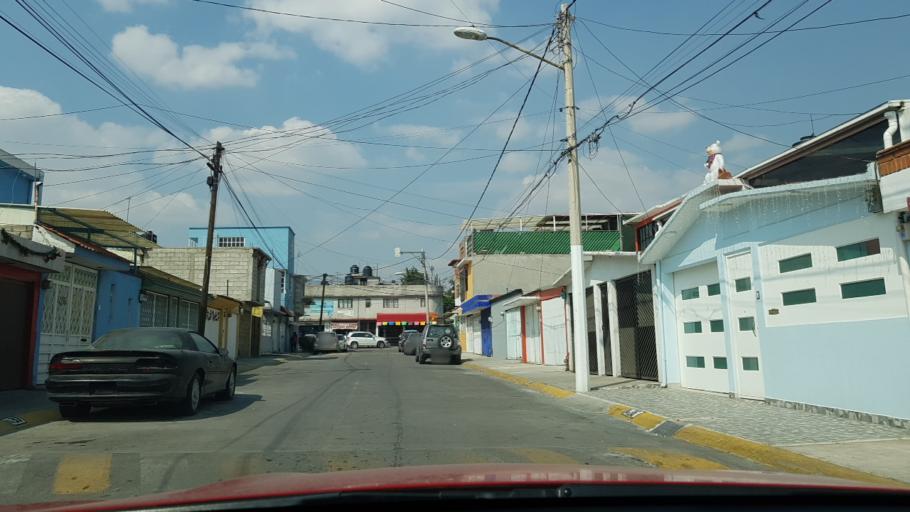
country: MX
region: Mexico
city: Cuautitlan Izcalli
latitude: 19.6444
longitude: -99.2108
